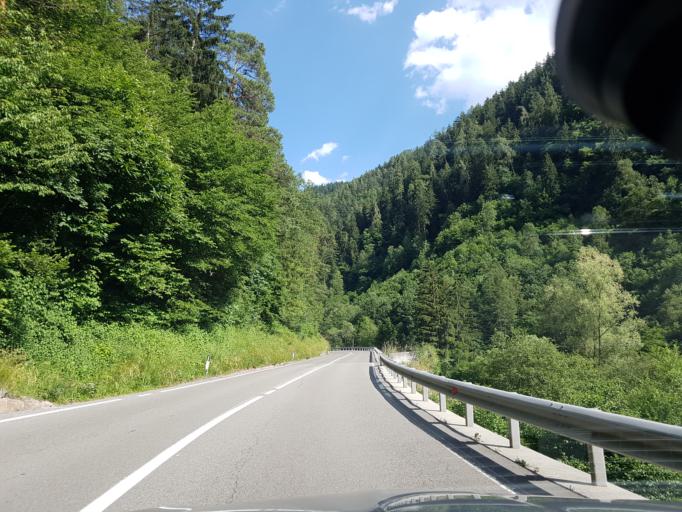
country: IT
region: Trentino-Alto Adige
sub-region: Bolzano
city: Laion
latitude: 46.5965
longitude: 11.5700
